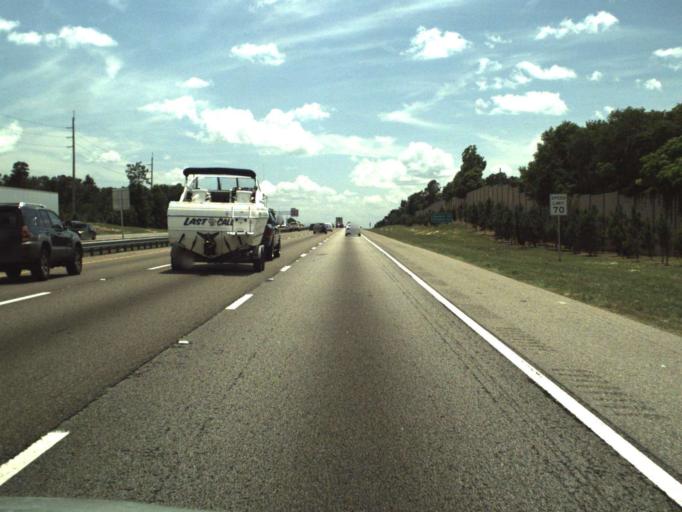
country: US
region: Florida
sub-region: Volusia County
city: Orange City
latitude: 28.9473
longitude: -81.2604
